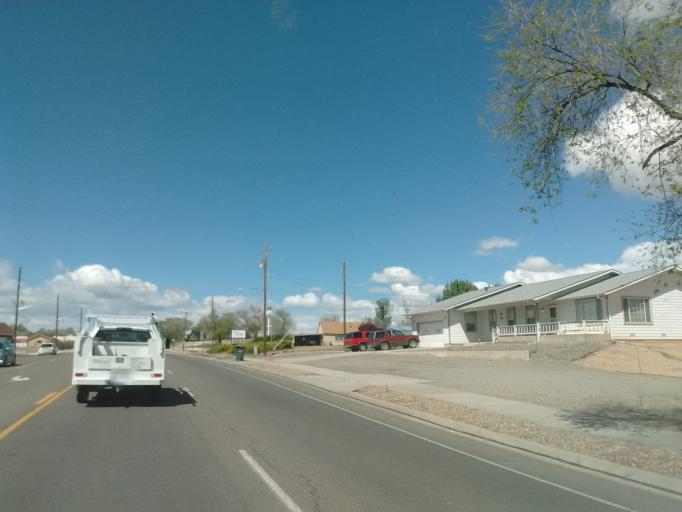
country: US
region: Colorado
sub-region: Mesa County
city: Fruitvale
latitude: 39.0919
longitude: -108.5198
